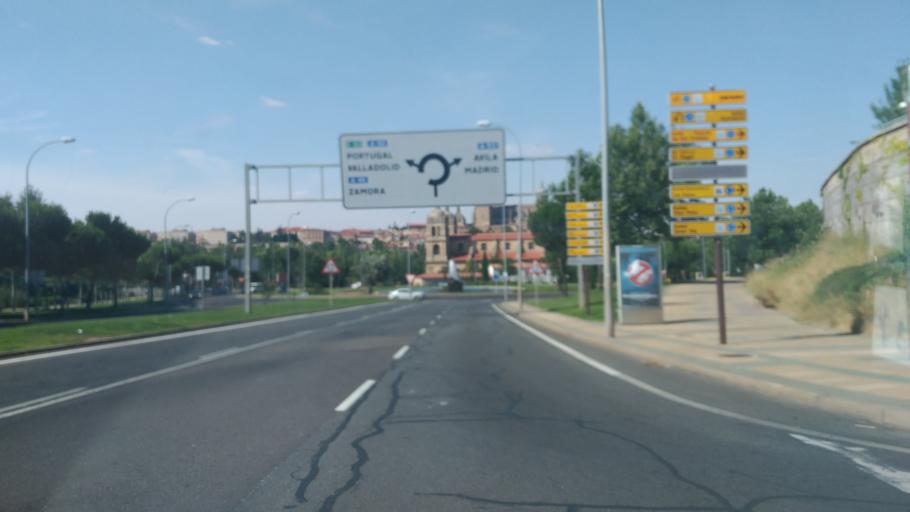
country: ES
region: Castille and Leon
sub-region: Provincia de Salamanca
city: Salamanca
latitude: 40.9528
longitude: -5.6698
